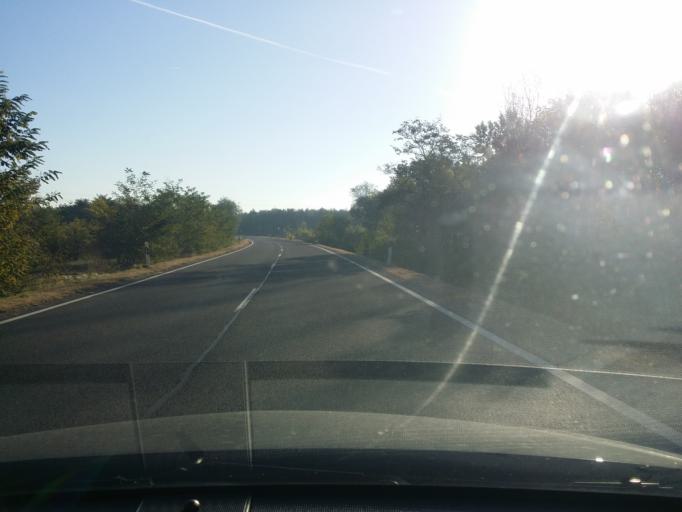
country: HU
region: Bacs-Kiskun
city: Nyarlorinc
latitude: 46.8624
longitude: 19.9353
